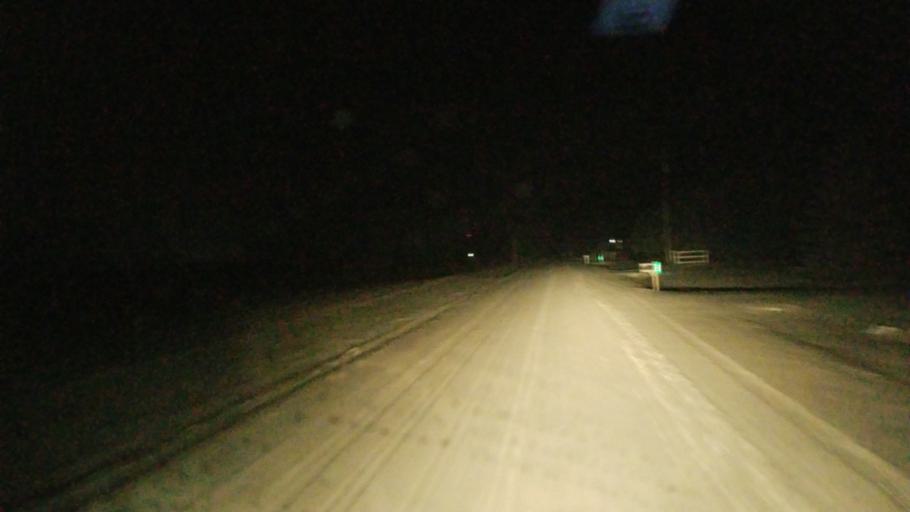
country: US
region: Michigan
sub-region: Osceola County
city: Reed City
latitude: 43.8238
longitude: -85.4141
